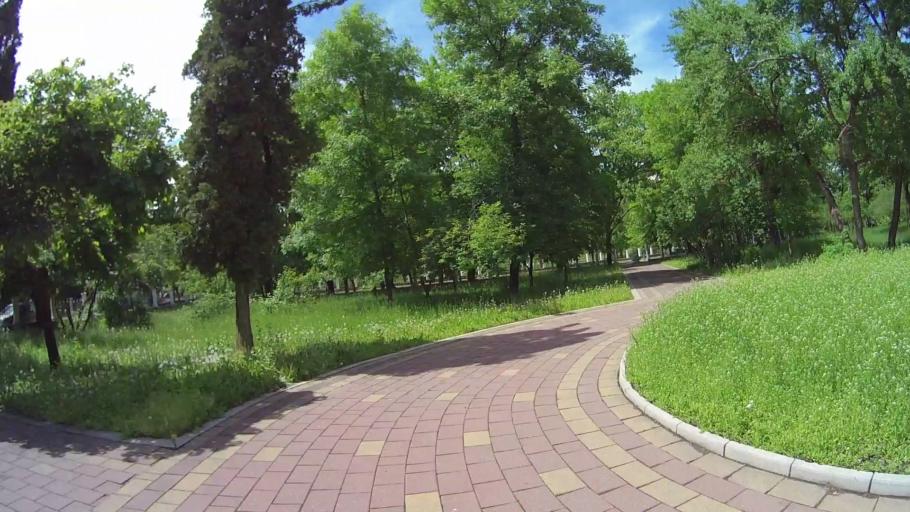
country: RU
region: Kabardino-Balkariya
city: Vol'nyy Aul
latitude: 43.4569
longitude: 43.5844
